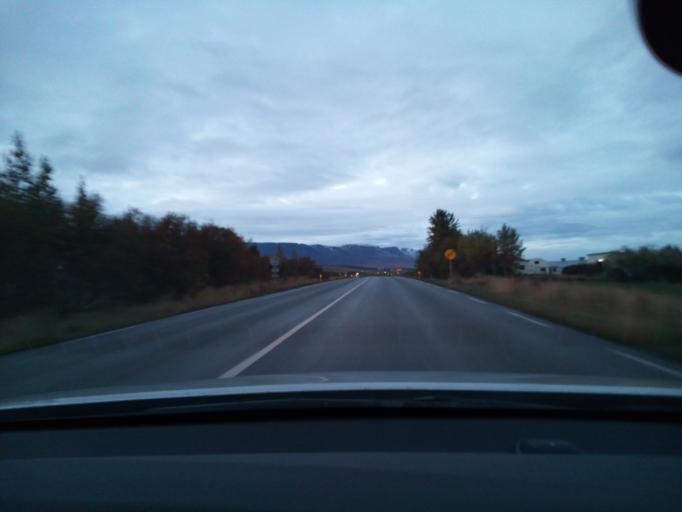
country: IS
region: Northeast
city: Akureyri
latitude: 65.7069
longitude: -18.1577
